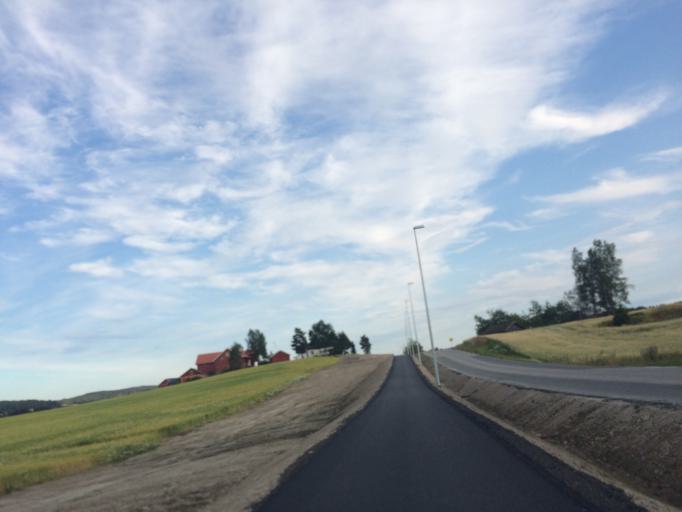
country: NO
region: Akershus
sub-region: Ski
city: Ski
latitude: 59.6948
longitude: 10.8590
